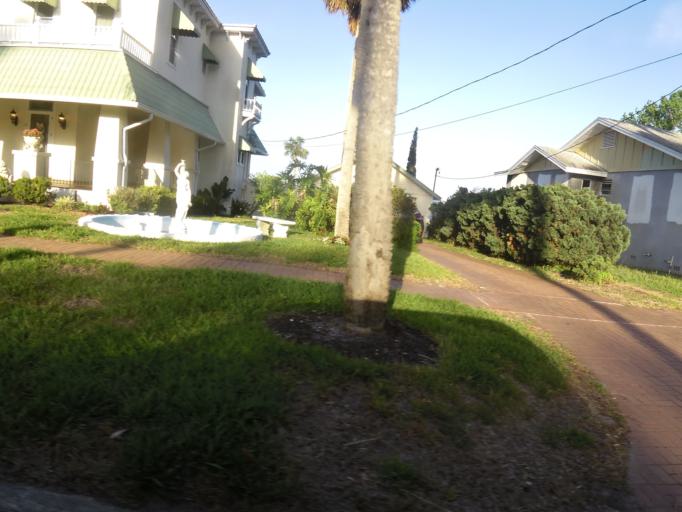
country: US
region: Florida
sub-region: Clay County
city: Green Cove Springs
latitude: 29.9944
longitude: -81.6771
